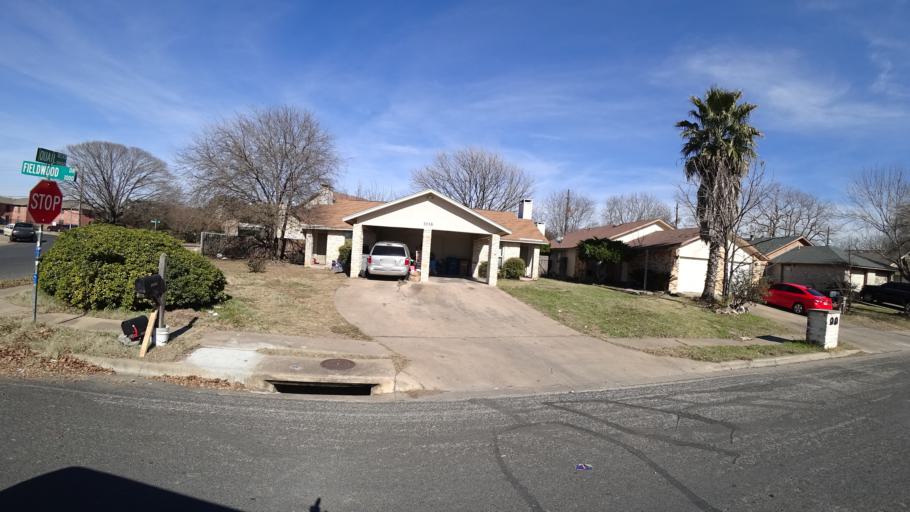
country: US
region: Texas
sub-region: Travis County
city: Wells Branch
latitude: 30.3714
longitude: -97.6993
